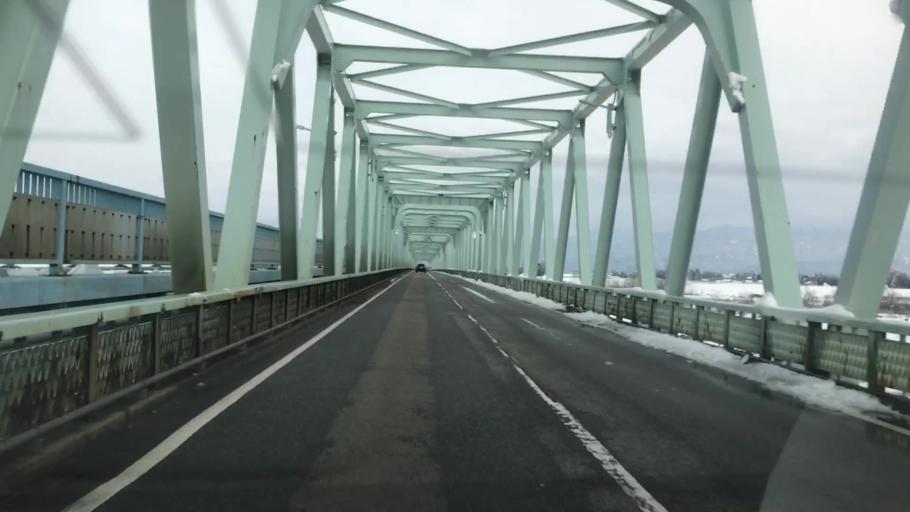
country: JP
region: Toyama
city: Toyama-shi
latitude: 36.6723
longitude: 137.2812
